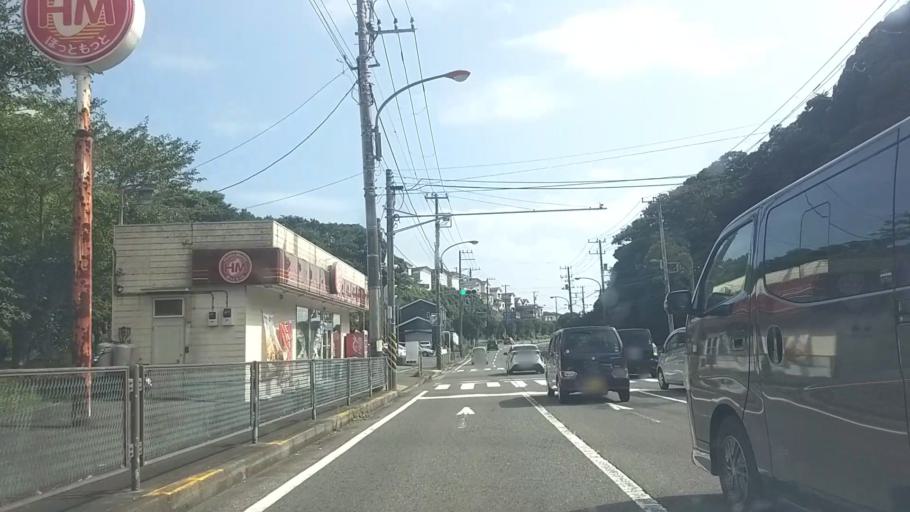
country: JP
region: Kanagawa
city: Yokosuka
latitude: 35.2234
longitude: 139.6845
